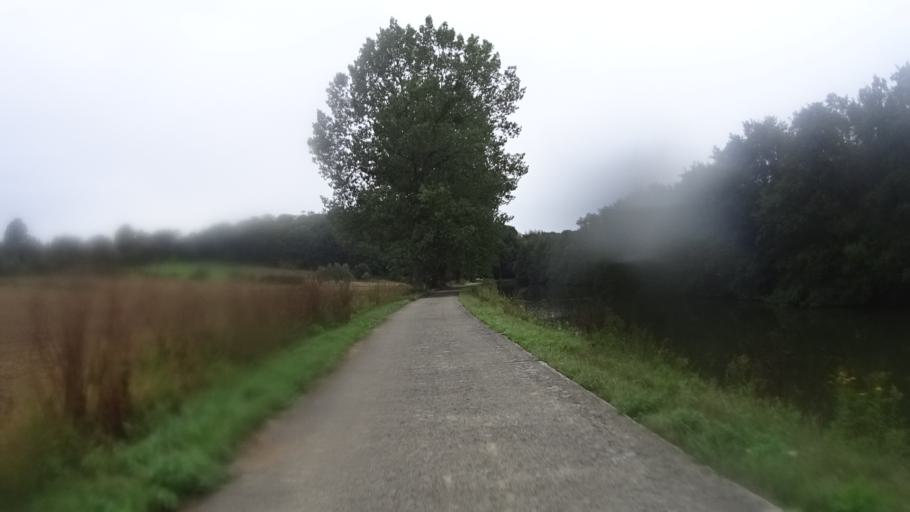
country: BE
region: Wallonia
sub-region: Province du Hainaut
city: Lobbes
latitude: 50.3456
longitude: 4.2483
